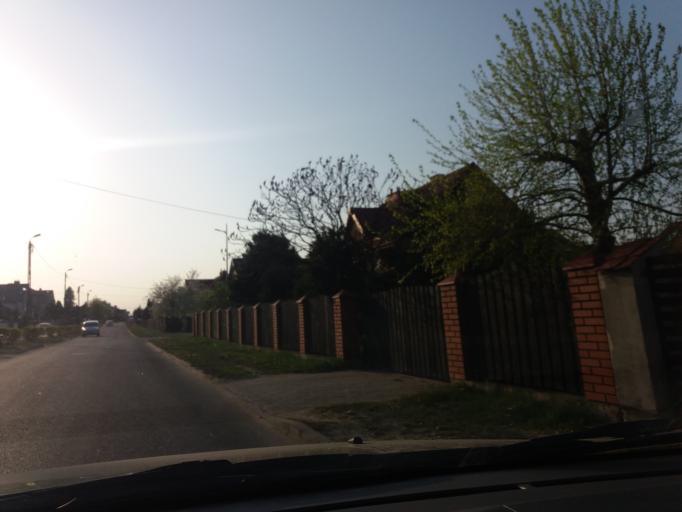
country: PL
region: Masovian Voivodeship
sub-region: Powiat mlawski
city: Mlawa
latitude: 53.1246
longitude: 20.3679
